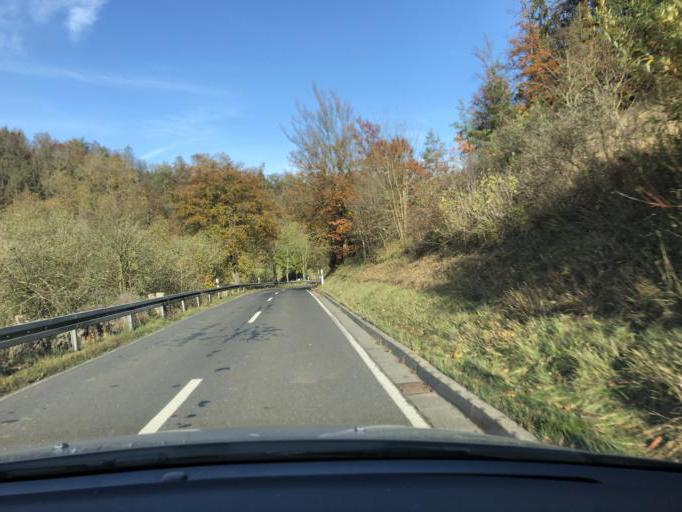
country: DE
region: Thuringia
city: Reurieth
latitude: 50.4460
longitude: 10.6452
